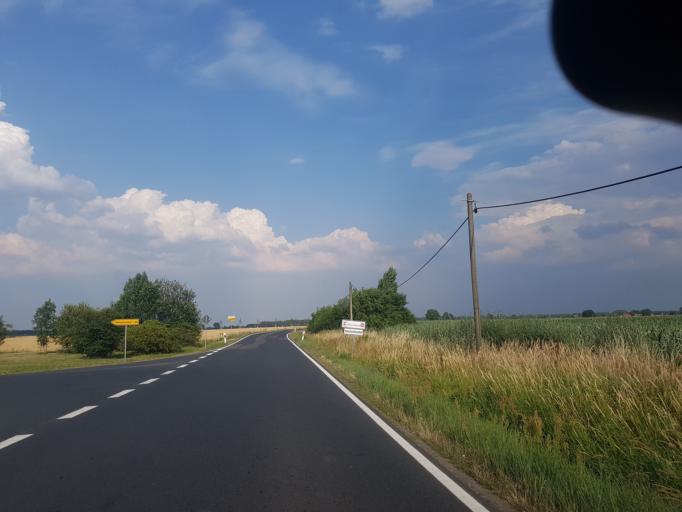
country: DE
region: Brandenburg
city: Herzberg
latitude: 51.6943
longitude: 13.2608
